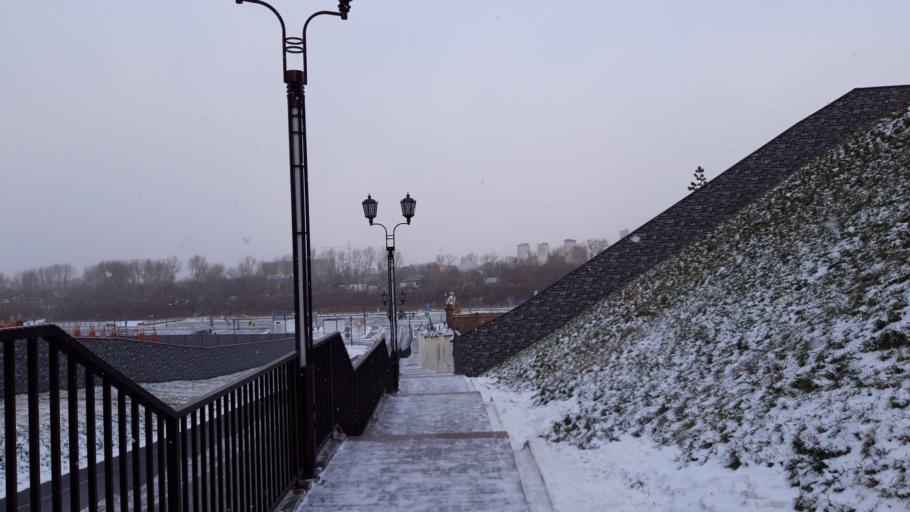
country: RU
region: Tjumen
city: Tyumen
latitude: 57.1609
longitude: 65.5507
